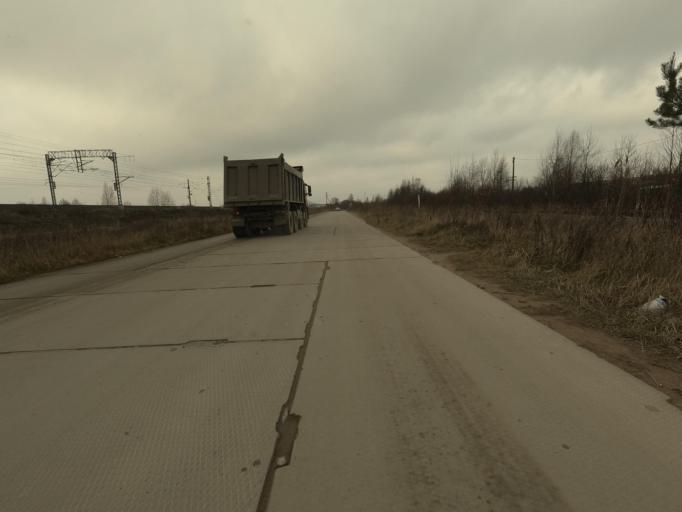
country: RU
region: Leningrad
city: Lyuban'
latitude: 59.4776
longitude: 31.2577
